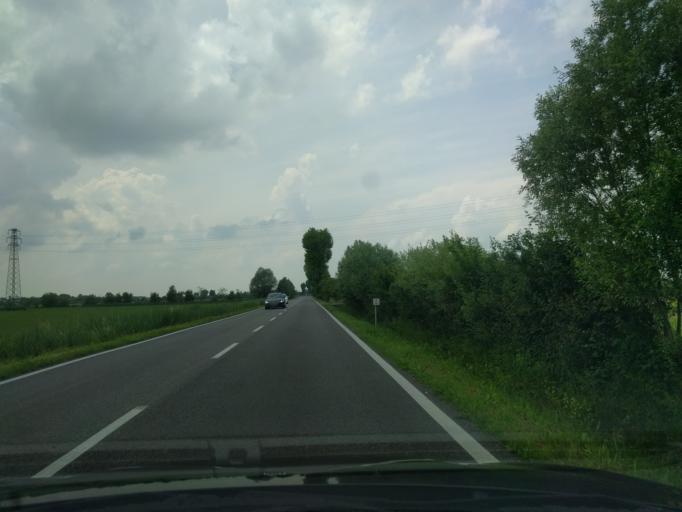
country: IT
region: Veneto
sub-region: Provincia di Rovigo
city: Lendinara
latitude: 45.0887
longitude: 11.5791
